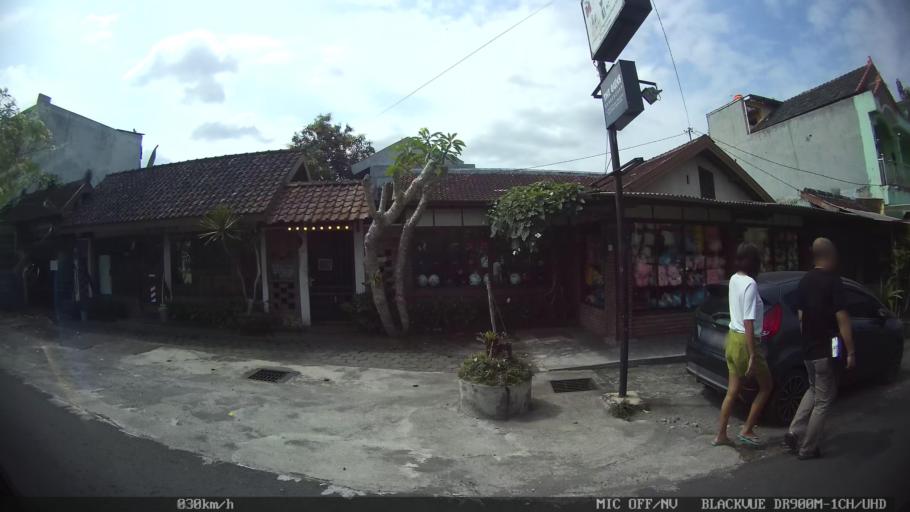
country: ID
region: Daerah Istimewa Yogyakarta
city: Depok
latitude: -7.7598
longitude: 110.4256
